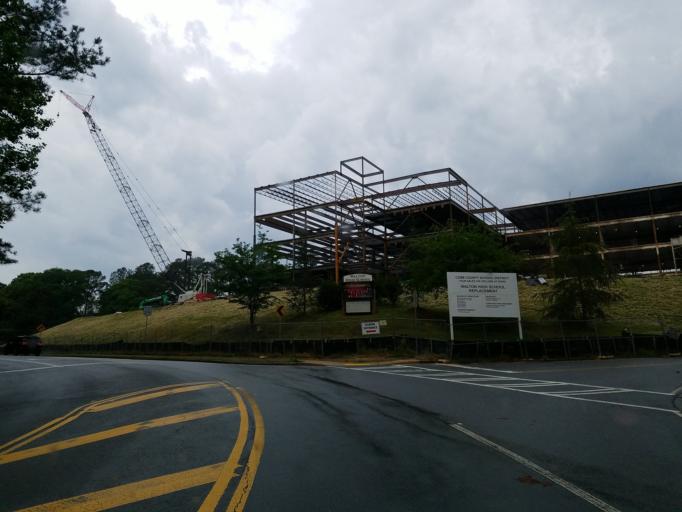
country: US
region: Georgia
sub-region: Fulton County
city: Roswell
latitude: 33.9880
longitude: -84.4392
